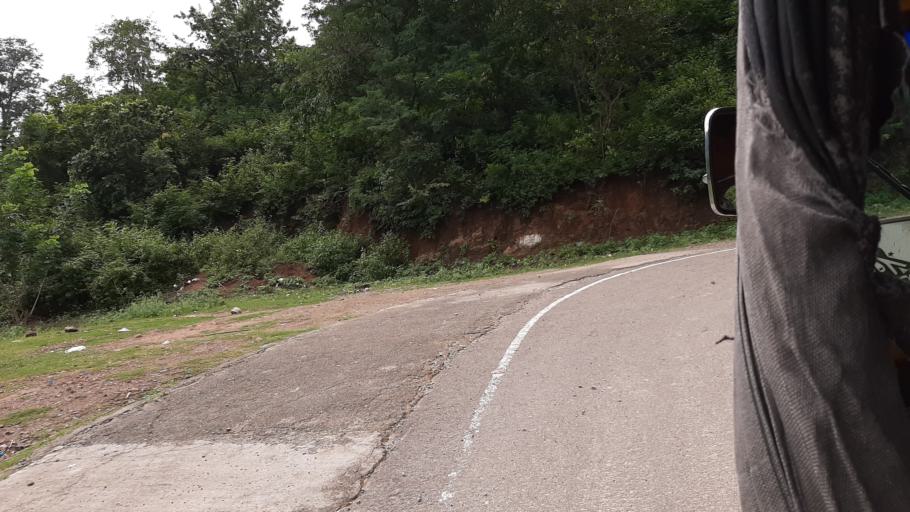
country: IN
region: Andhra Pradesh
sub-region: Vizianagaram District
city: Salur
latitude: 18.2767
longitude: 83.0371
